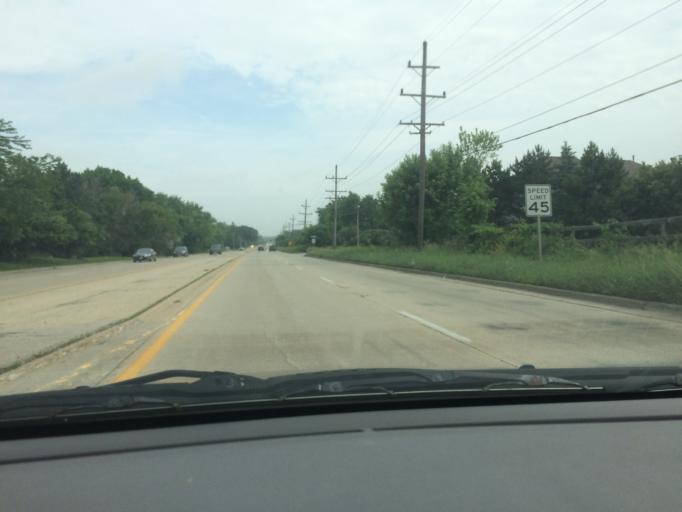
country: US
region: Illinois
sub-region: DuPage County
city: Wayne
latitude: 41.9575
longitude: -88.2056
